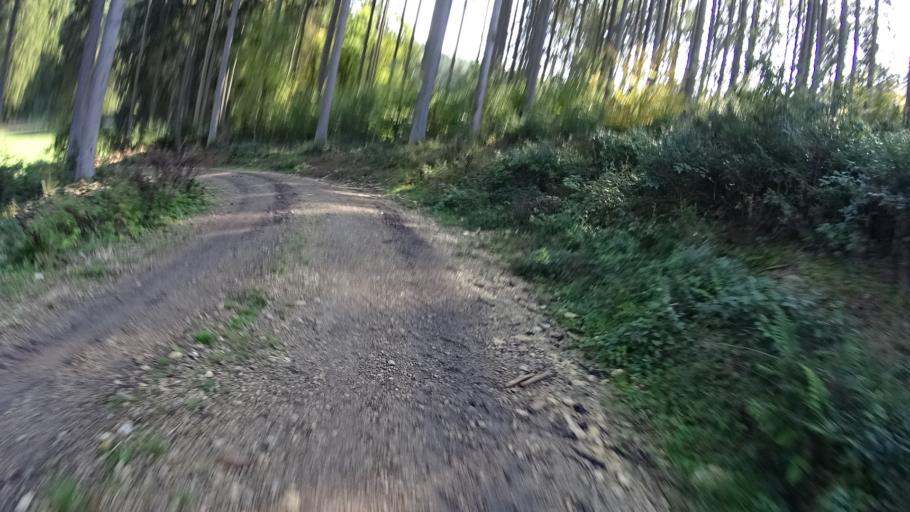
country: DE
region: Bavaria
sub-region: Upper Bavaria
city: Bohmfeld
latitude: 48.8753
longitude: 11.3626
